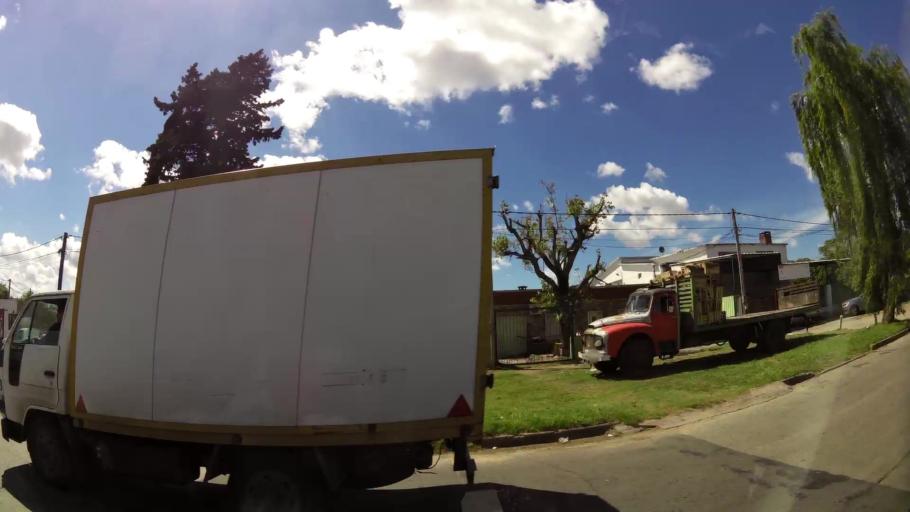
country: UY
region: Canelones
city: Paso de Carrasco
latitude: -34.8329
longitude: -56.1287
